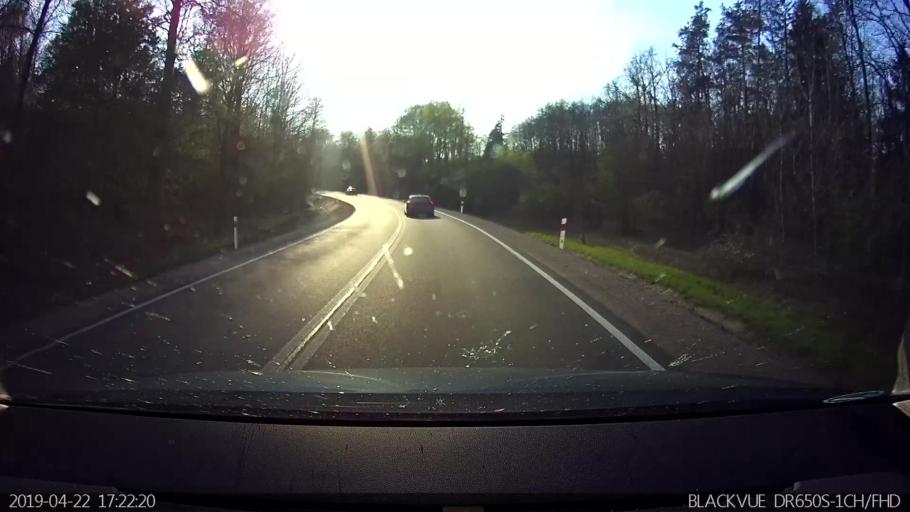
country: PL
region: Masovian Voivodeship
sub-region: Powiat sokolowski
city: Repki
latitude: 52.3911
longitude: 22.3411
